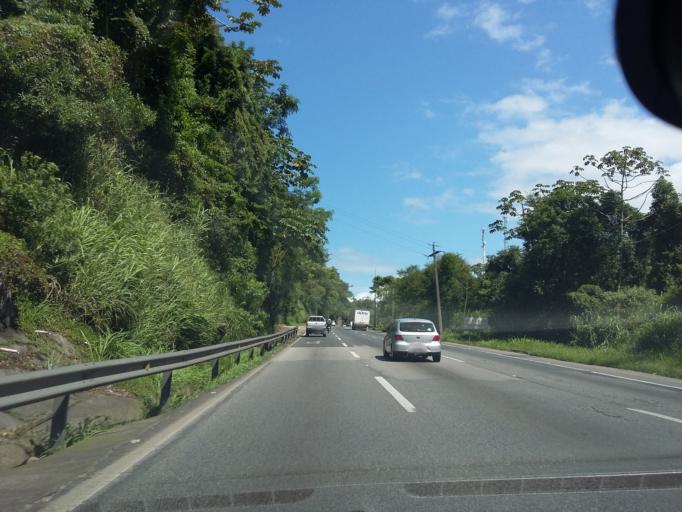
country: BR
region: Santa Catarina
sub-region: Itapema
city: Itapema
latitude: -27.0389
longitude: -48.6001
